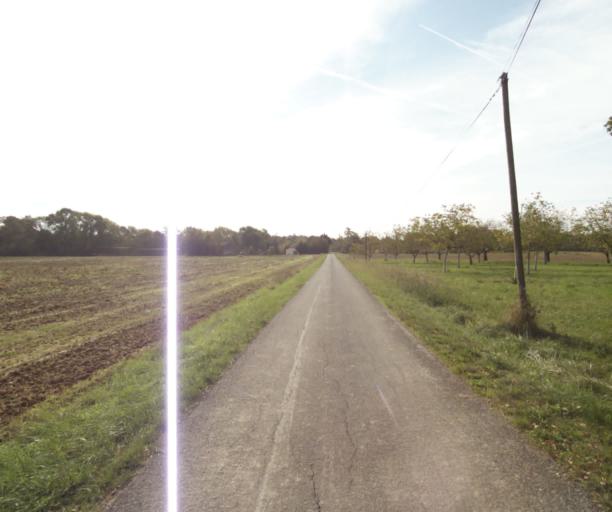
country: FR
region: Midi-Pyrenees
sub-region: Departement du Tarn-et-Garonne
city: Orgueil
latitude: 43.8938
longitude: 1.4131
